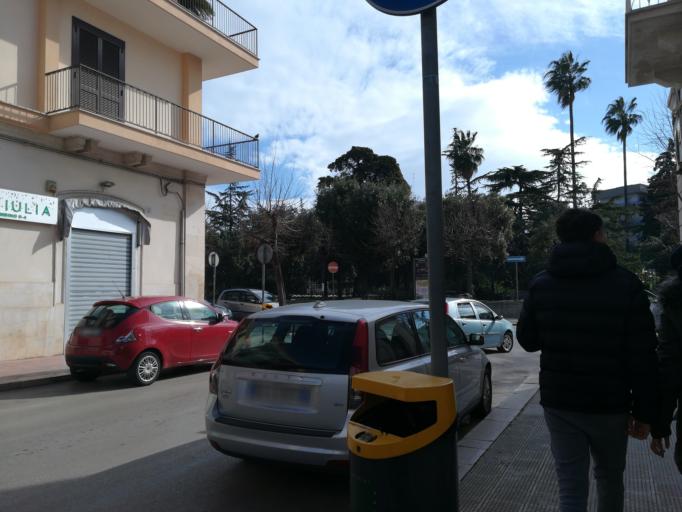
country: IT
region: Apulia
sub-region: Provincia di Bari
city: Bitonto
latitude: 41.1120
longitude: 16.6948
